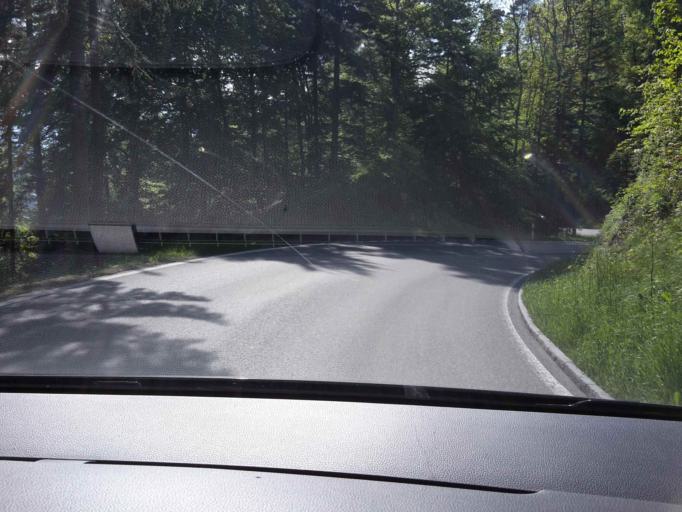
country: CH
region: Bern
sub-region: Thun District
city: Hilterfingen
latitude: 46.7544
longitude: 7.6477
